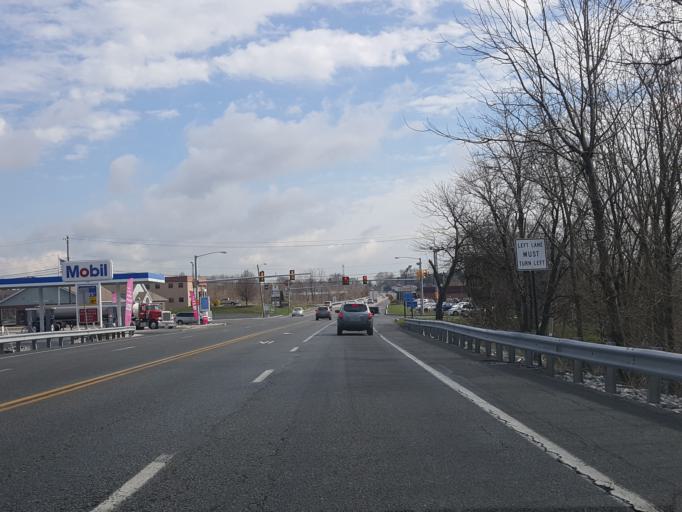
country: US
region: Pennsylvania
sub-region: Lebanon County
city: Avon
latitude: 40.3477
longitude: -76.3875
